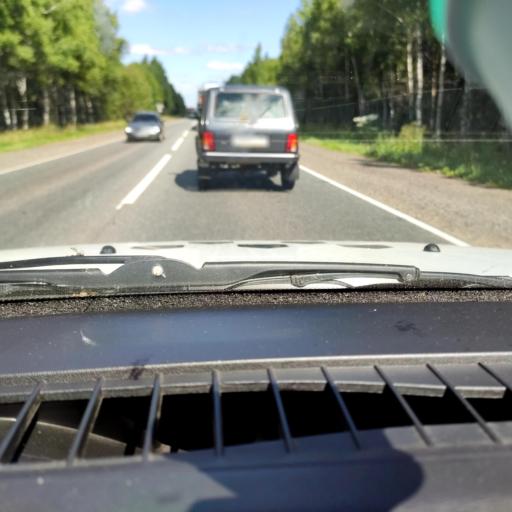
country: RU
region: Udmurtiya
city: Votkinsk
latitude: 56.9781
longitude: 53.7602
